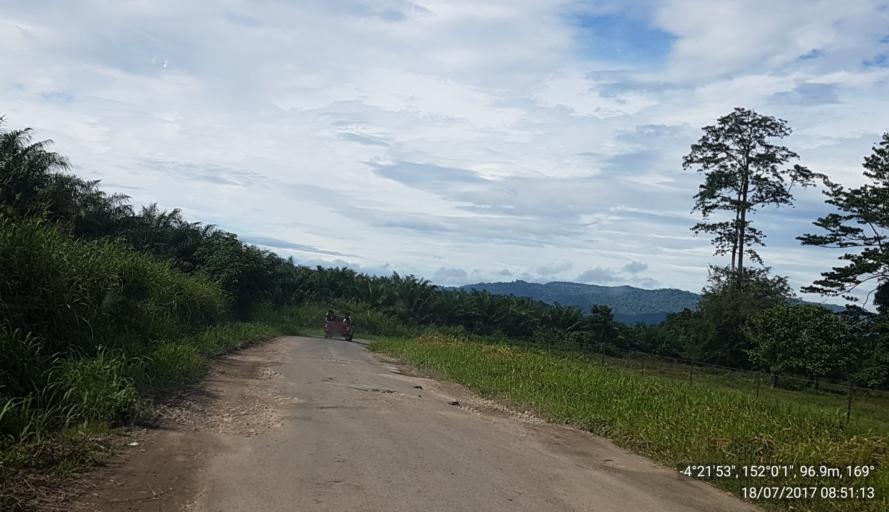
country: PG
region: East New Britain
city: Rabaul
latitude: -4.3647
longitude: 152.0006
